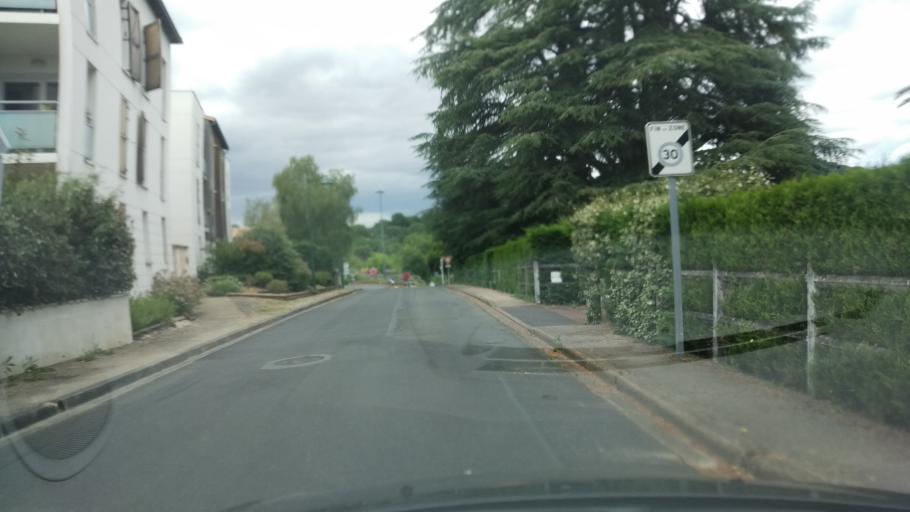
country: FR
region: Poitou-Charentes
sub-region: Departement de la Vienne
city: Vouneuil-sous-Biard
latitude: 46.5767
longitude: 0.2735
